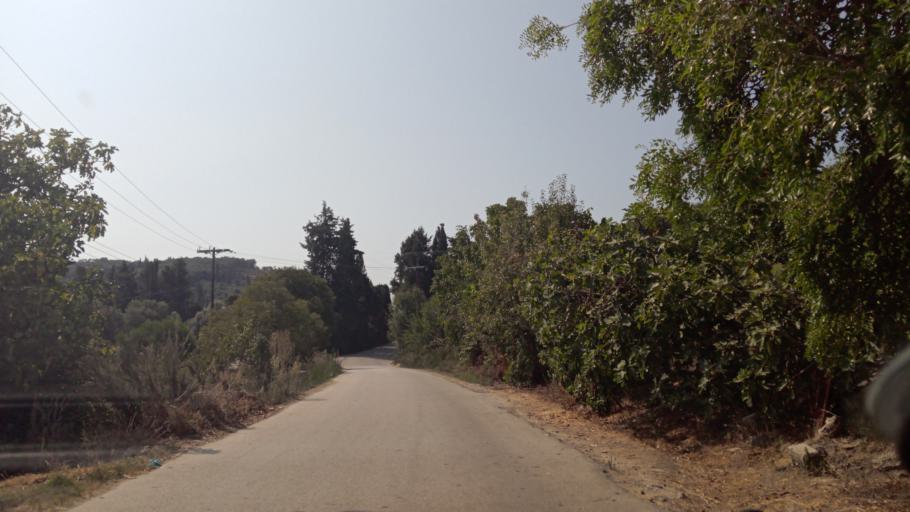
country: GR
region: Ionian Islands
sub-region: Nomos Kerkyras
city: Perivoli
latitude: 39.4028
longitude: 20.0266
